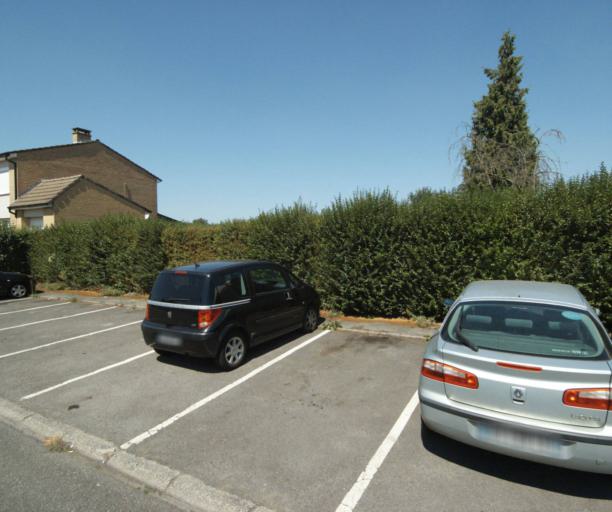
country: FR
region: Nord-Pas-de-Calais
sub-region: Departement du Nord
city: Halluin
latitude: 50.7812
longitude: 3.1126
